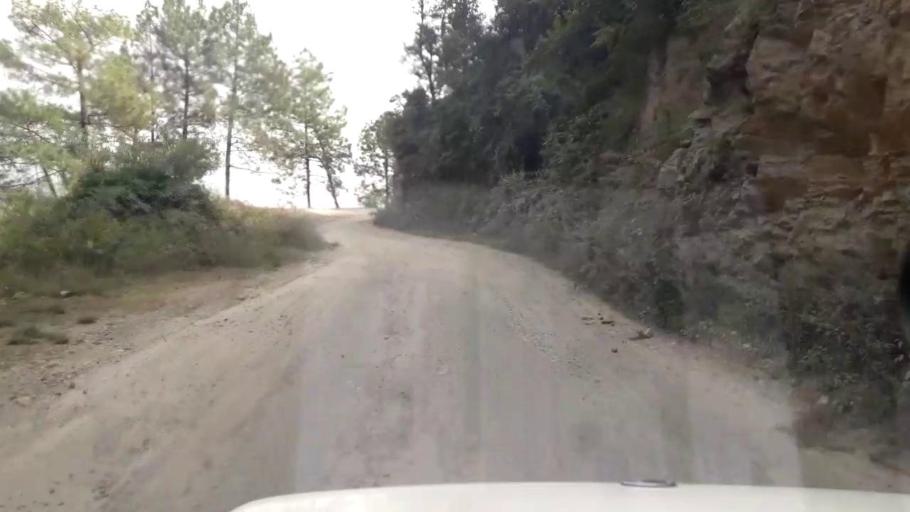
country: IN
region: Himachal Pradesh
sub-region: Shimla
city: Shimla
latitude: 31.0571
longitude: 77.1564
